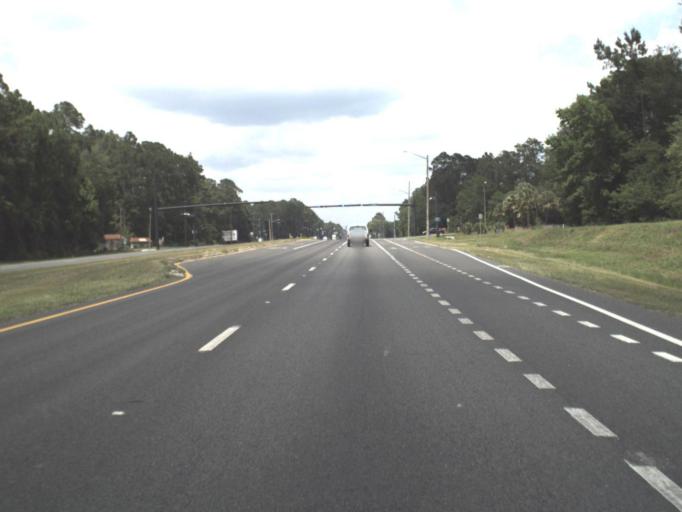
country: US
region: Florida
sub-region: Alachua County
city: Gainesville
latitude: 29.6985
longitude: -82.2799
